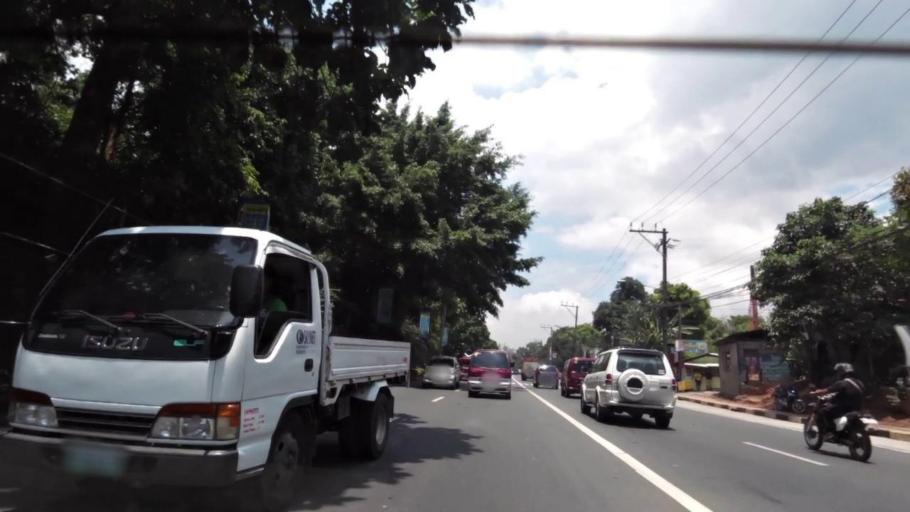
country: PH
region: Calabarzon
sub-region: Province of Rizal
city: Antipolo
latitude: 14.6045
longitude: 121.1746
